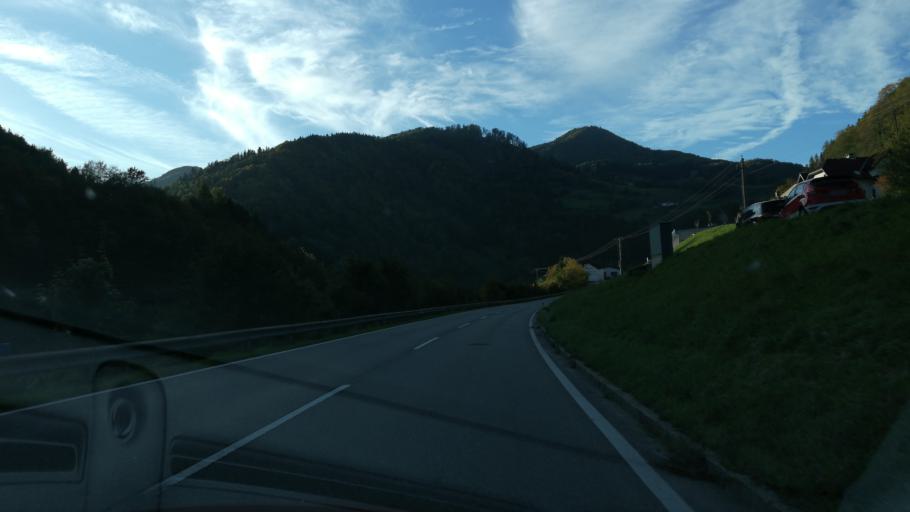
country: AT
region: Upper Austria
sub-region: Politischer Bezirk Steyr-Land
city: Reichraming
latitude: 47.8997
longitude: 14.4577
